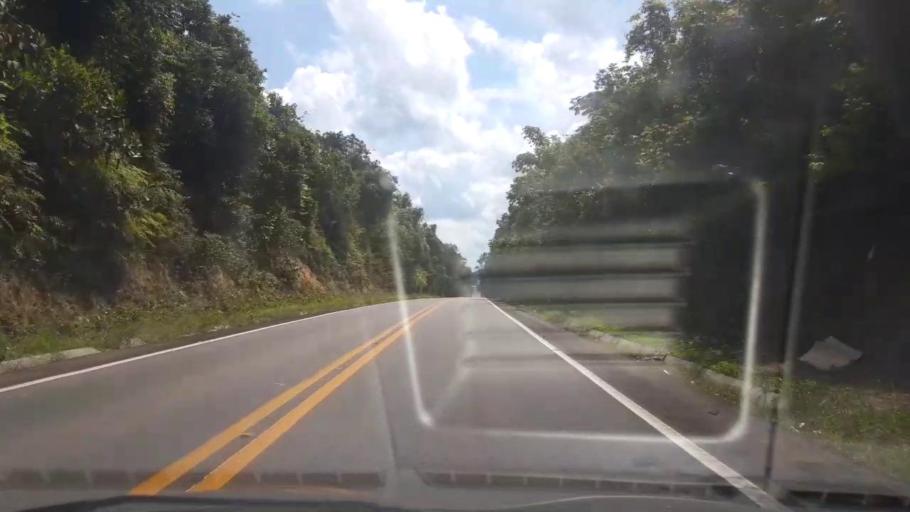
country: BR
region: Amazonas
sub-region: Rio Preto Da Eva
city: Rio Preto da Eva
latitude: -2.4967
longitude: -60.0350
